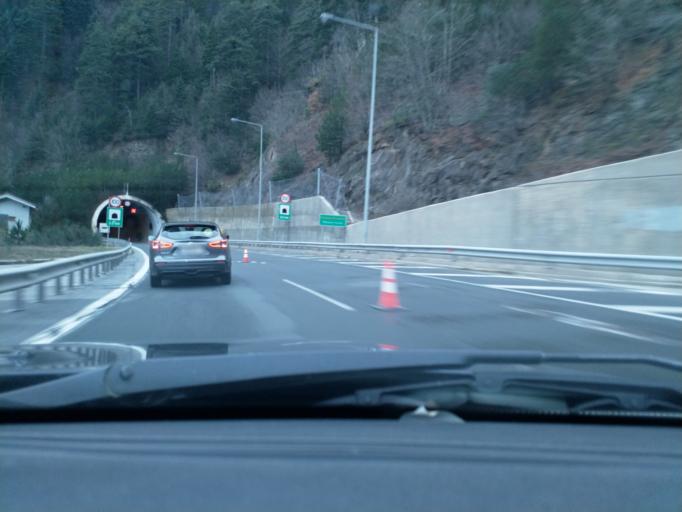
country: GR
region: Epirus
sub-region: Nomos Ioanninon
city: Metsovo
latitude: 39.7736
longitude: 21.2468
